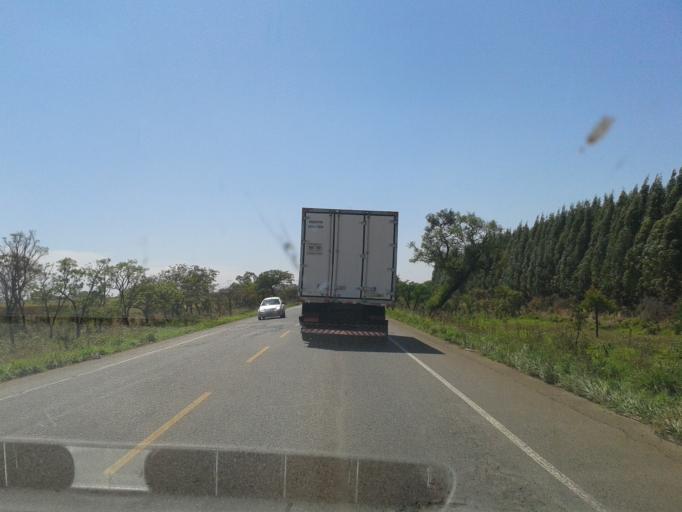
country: BR
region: Minas Gerais
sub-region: Patrocinio
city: Patrocinio
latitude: -19.2815
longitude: -47.4321
